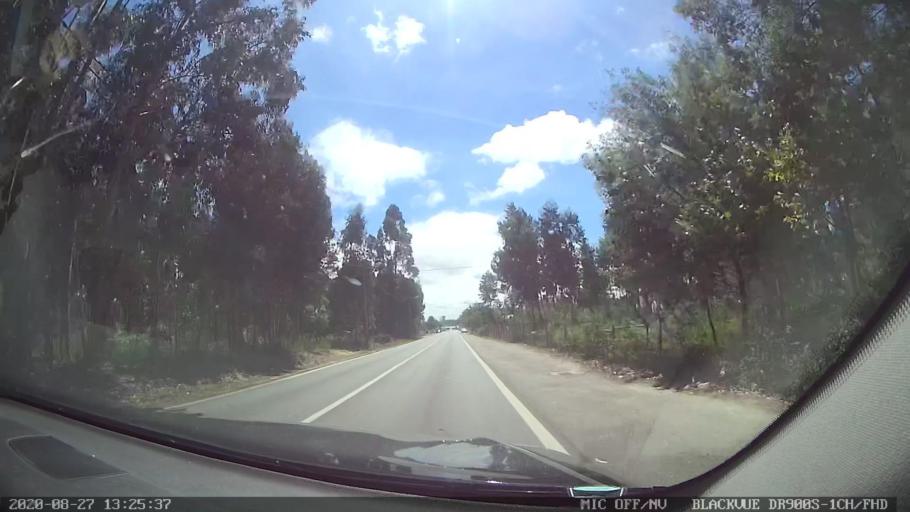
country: PT
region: Aveiro
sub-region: Vagos
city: Vagos
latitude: 40.5450
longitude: -8.6785
